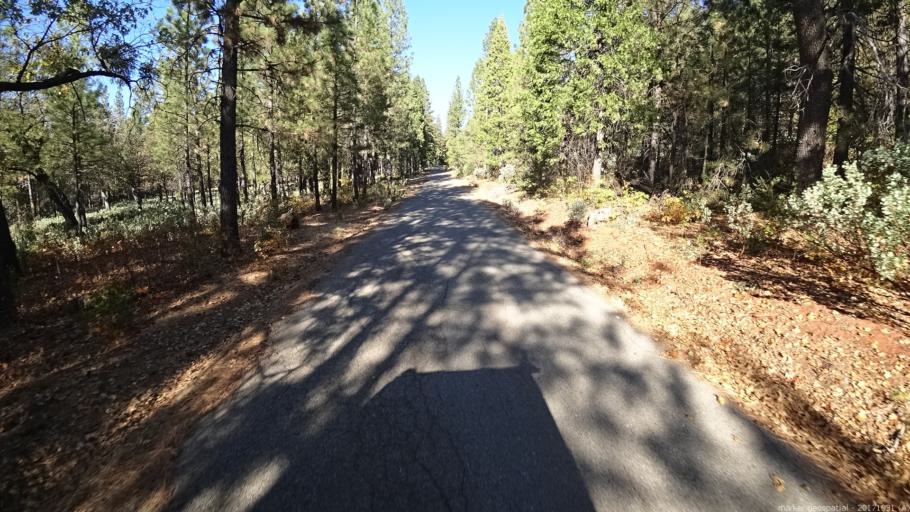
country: US
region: California
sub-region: Shasta County
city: Shingletown
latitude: 40.4860
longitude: -121.9273
